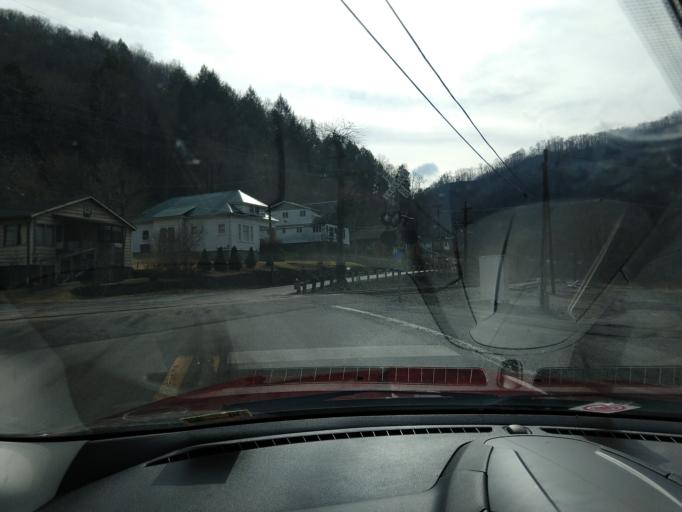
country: US
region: West Virginia
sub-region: McDowell County
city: Welch
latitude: 37.3336
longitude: -81.7172
